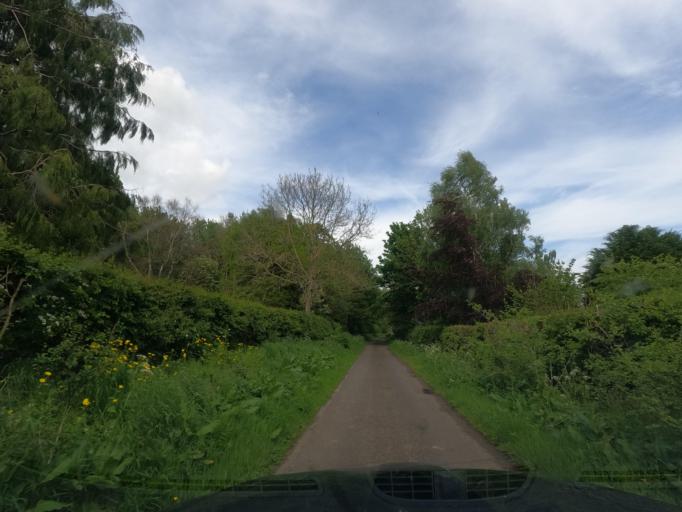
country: GB
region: England
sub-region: Northumberland
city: Kirknewton
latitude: 55.5672
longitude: -2.1013
